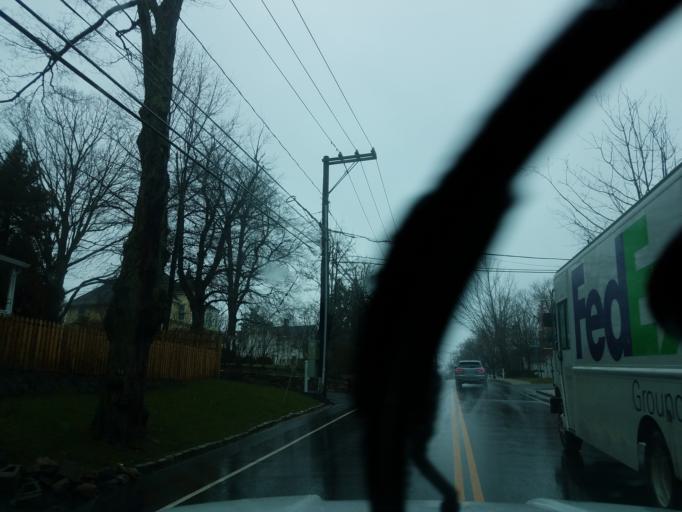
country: US
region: Connecticut
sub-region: Fairfield County
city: Darien
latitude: 41.0642
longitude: -73.4884
